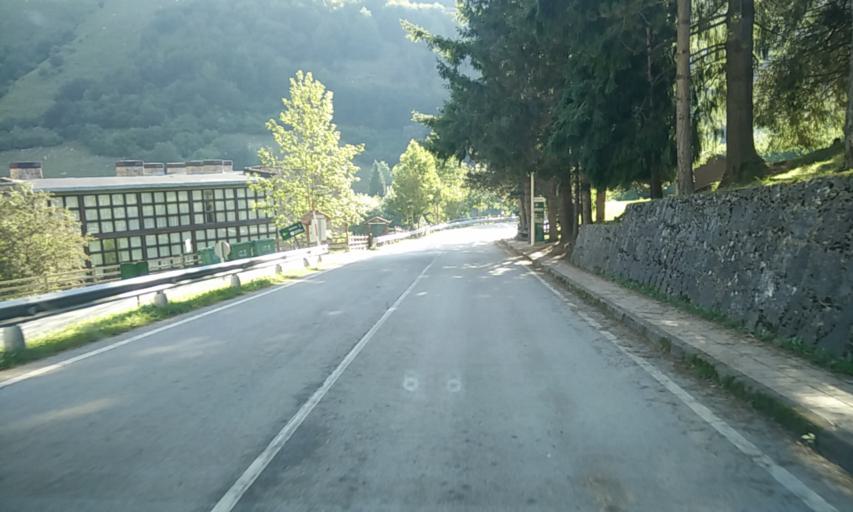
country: ES
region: Castille and Leon
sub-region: Provincia de Leon
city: Posada de Valdeon
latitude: 43.1443
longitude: -4.8121
